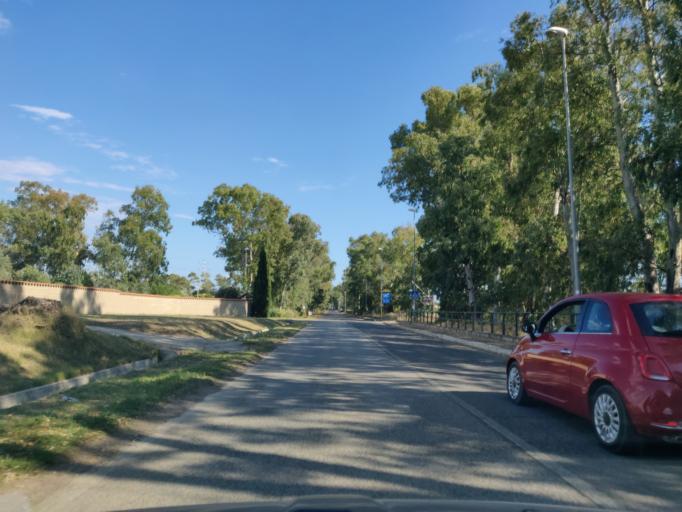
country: IT
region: Latium
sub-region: Citta metropolitana di Roma Capitale
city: Aurelia
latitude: 42.1497
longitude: 11.7596
